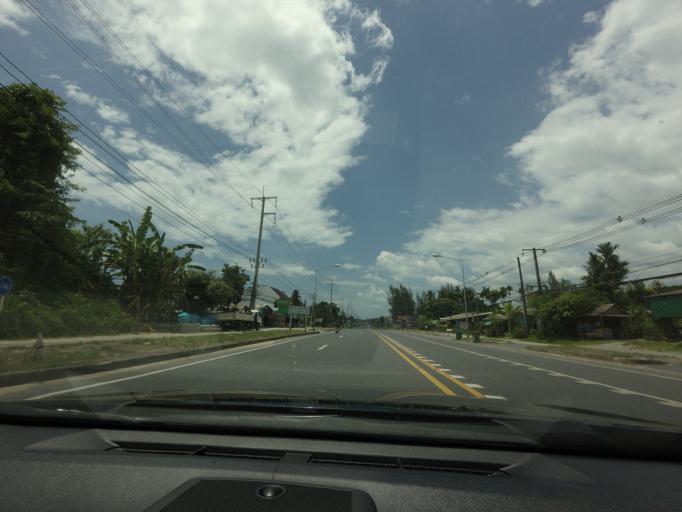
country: TH
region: Phangnga
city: Ban Khao Lak
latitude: 8.6594
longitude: 98.2533
